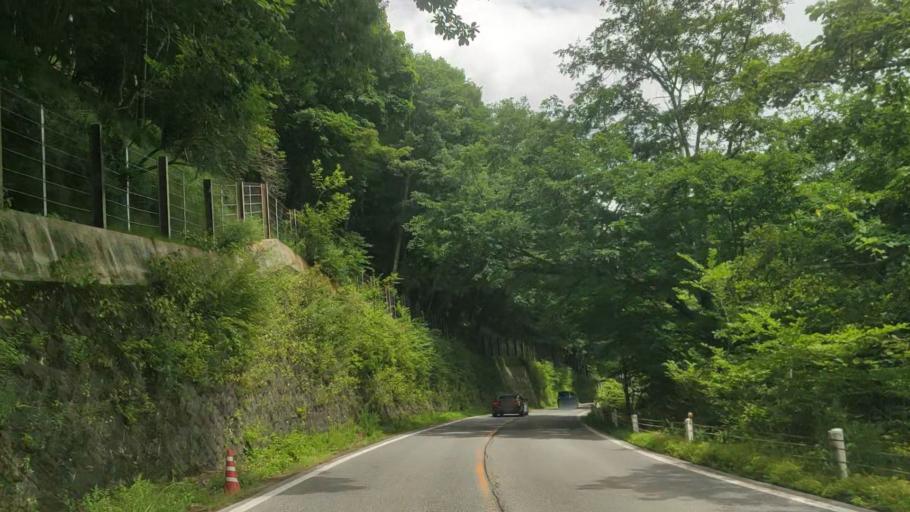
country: JP
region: Tochigi
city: Nikko
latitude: 36.7956
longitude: 139.4303
